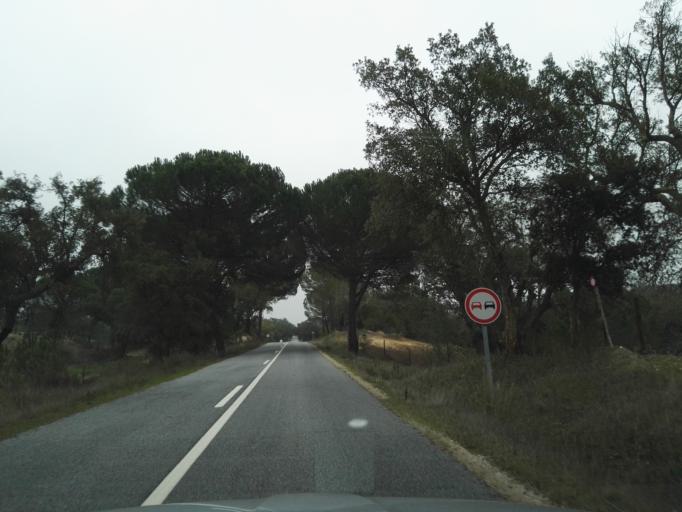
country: PT
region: Evora
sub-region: Vendas Novas
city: Vendas Novas
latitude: 38.7647
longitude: -8.4104
